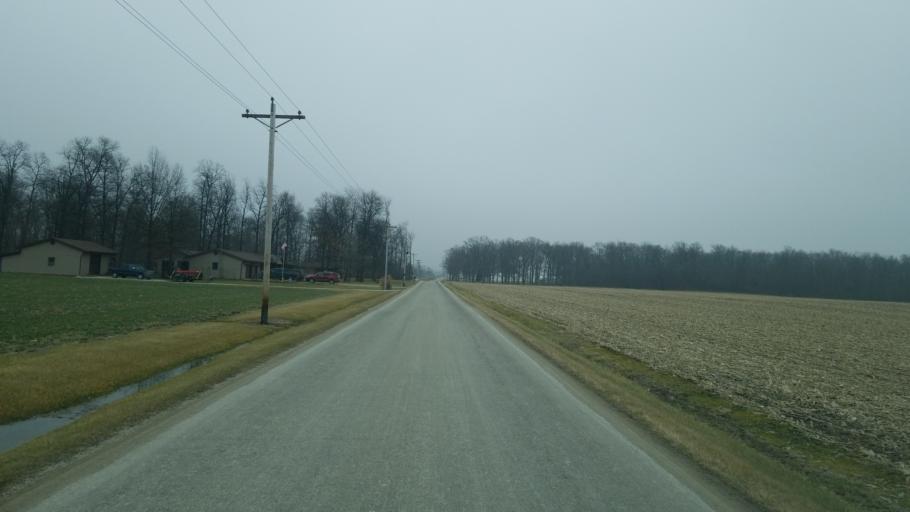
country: US
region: Indiana
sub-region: Adams County
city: Geneva
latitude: 40.5564
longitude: -84.9103
